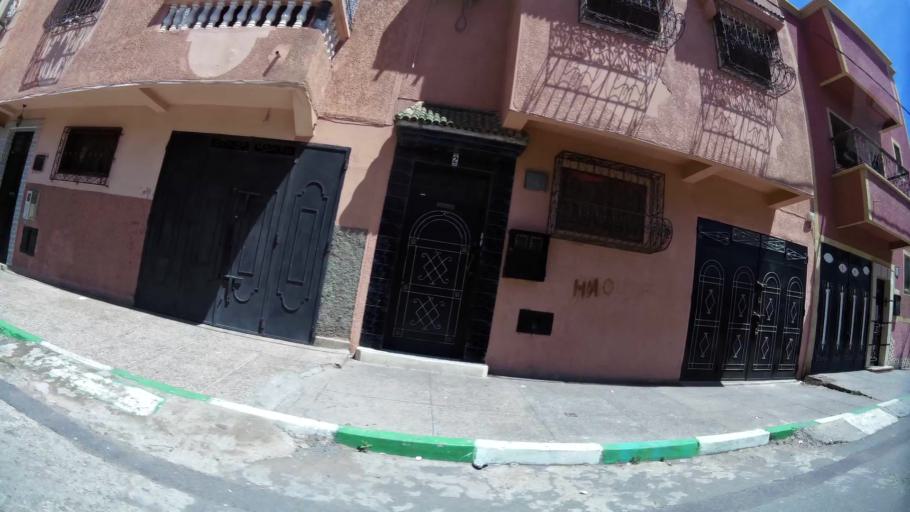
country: MA
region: Marrakech-Tensift-Al Haouz
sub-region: Marrakech
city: Marrakesh
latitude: 31.6391
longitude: -8.0547
